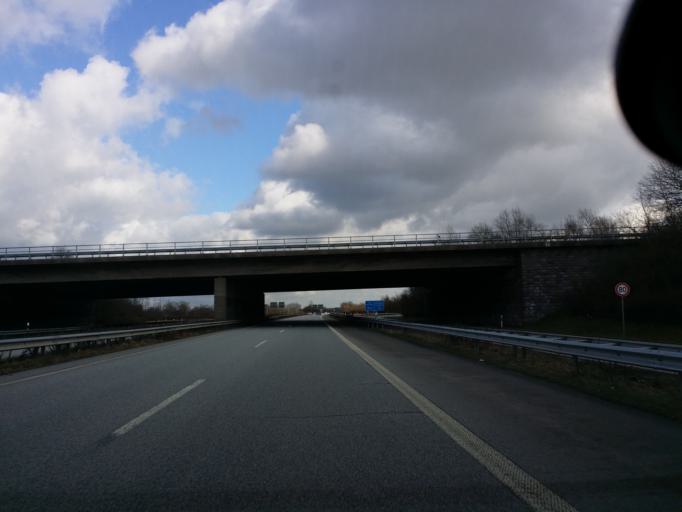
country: DE
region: Schleswig-Holstein
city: Schulldorf
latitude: 54.3051
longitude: 9.7535
